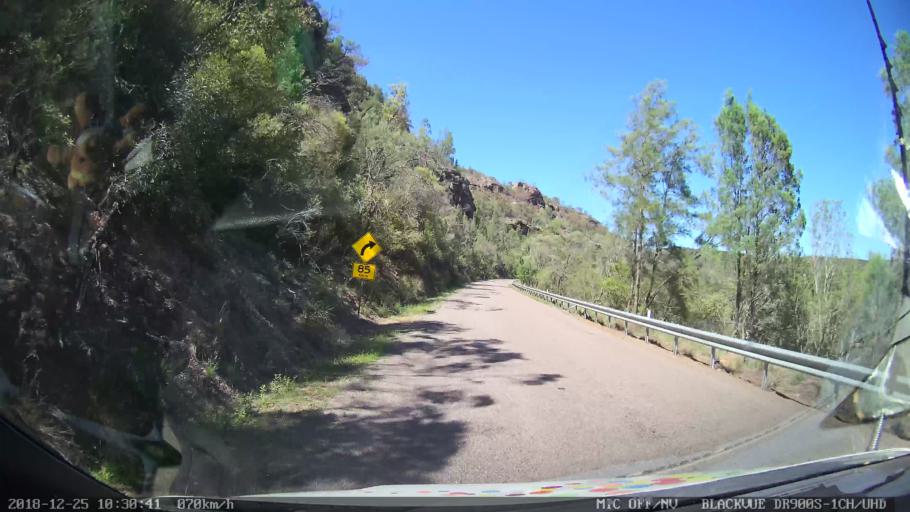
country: AU
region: New South Wales
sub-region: Muswellbrook
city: Denman
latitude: -32.3836
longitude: 150.4359
